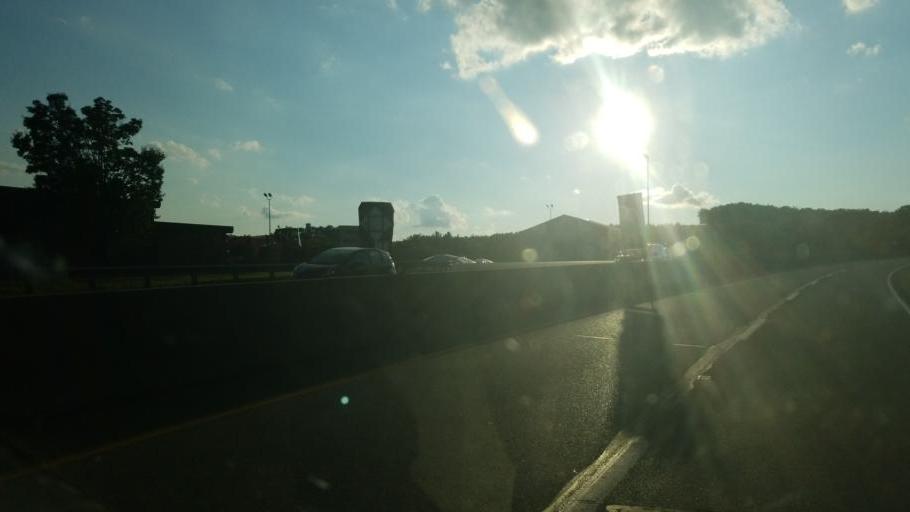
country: US
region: Pennsylvania
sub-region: Beaver County
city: Big Beaver
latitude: 40.8201
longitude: -80.3417
